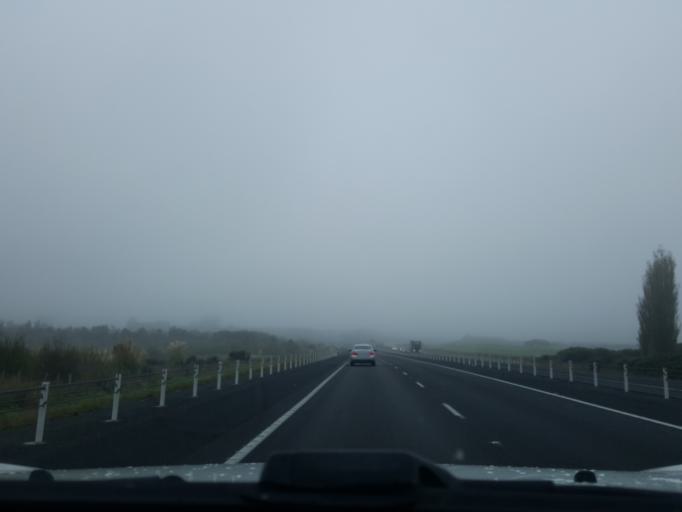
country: NZ
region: Waikato
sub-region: Waikato District
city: Ngaruawahia
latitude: -37.6943
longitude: 175.2130
